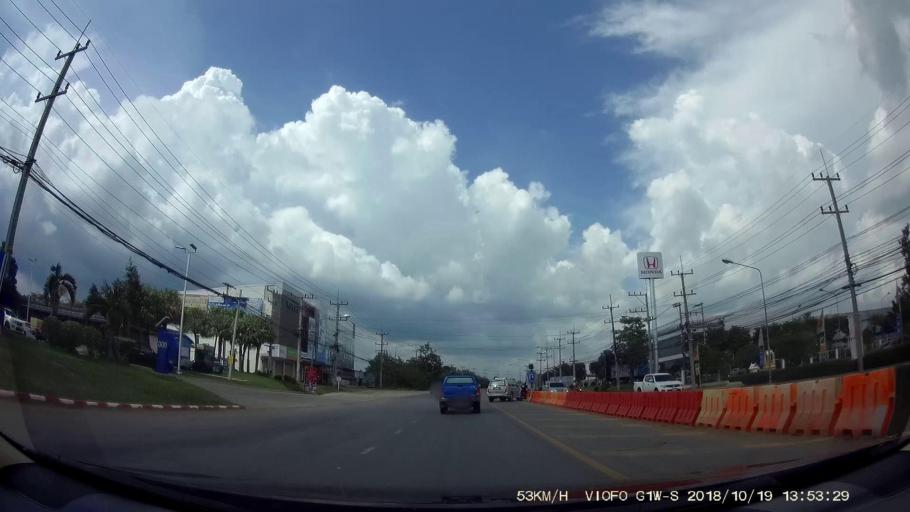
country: TH
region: Chaiyaphum
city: Chaiyaphum
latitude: 15.7779
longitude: 102.0253
